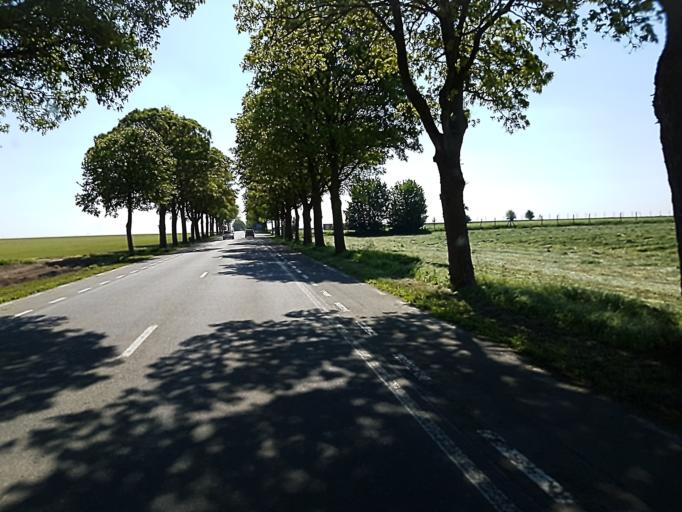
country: BE
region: Wallonia
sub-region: Province du Hainaut
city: Brugelette
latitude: 50.5753
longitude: 3.8676
